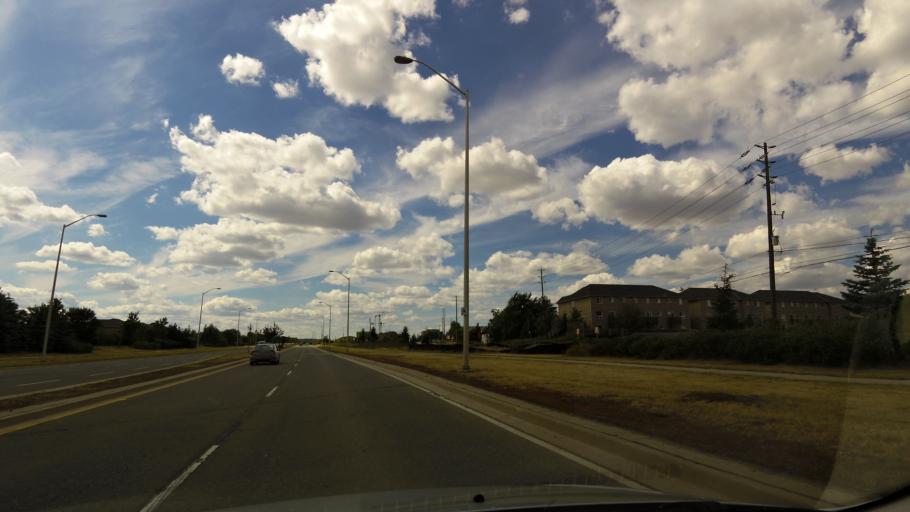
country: CA
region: Ontario
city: Burlington
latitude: 43.4289
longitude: -79.7674
